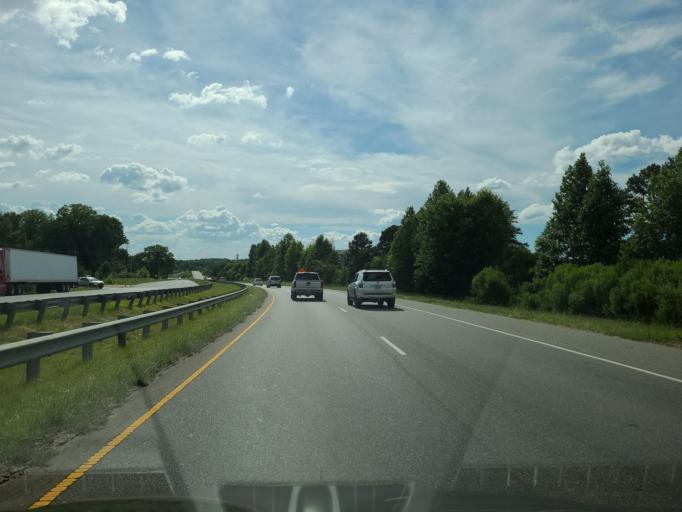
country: US
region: North Carolina
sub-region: Mecklenburg County
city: Charlotte
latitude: 35.2844
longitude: -80.7657
